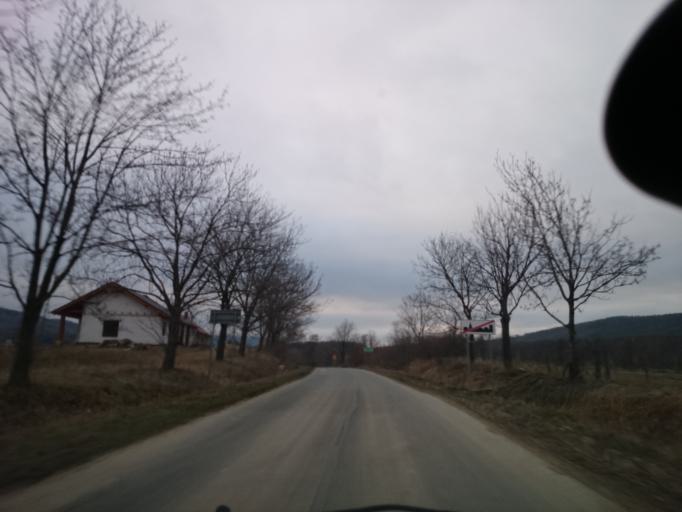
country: PL
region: Lower Silesian Voivodeship
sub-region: Powiat zabkowicki
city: Bardo
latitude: 50.5408
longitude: 16.7299
